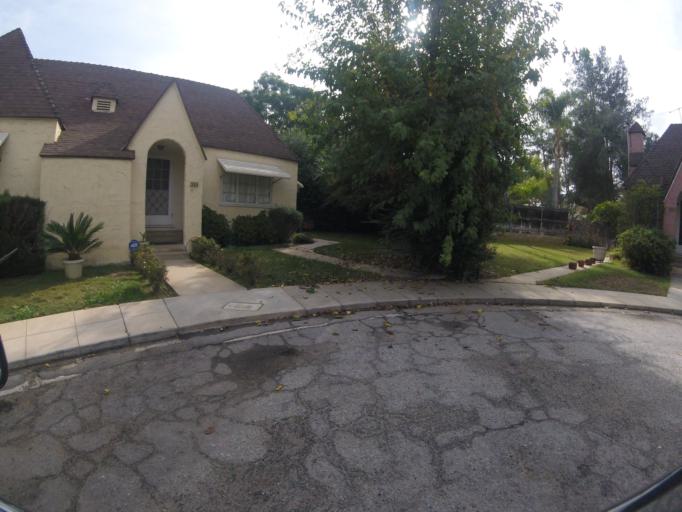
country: US
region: California
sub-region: San Bernardino County
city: Redlands
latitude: 34.0474
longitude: -117.1859
